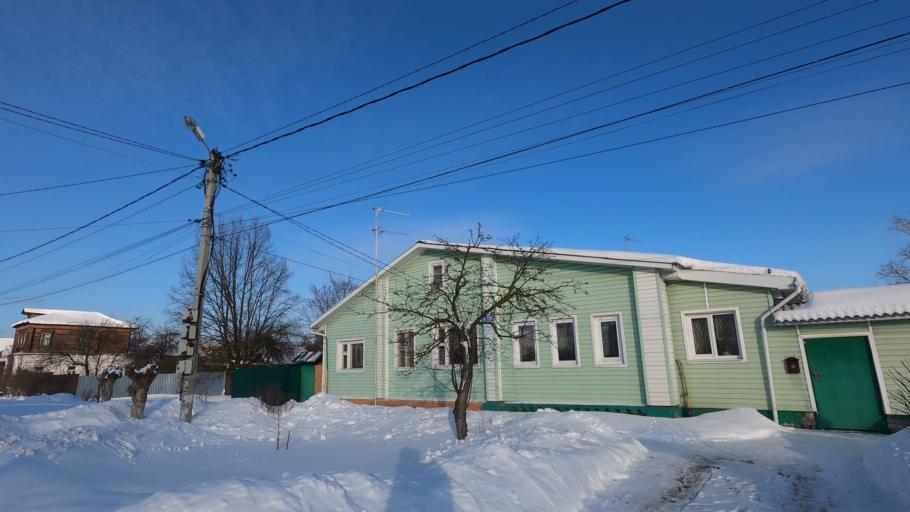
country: RU
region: Moskovskaya
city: Pavlovskiy Posad
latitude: 55.7677
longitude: 38.6986
